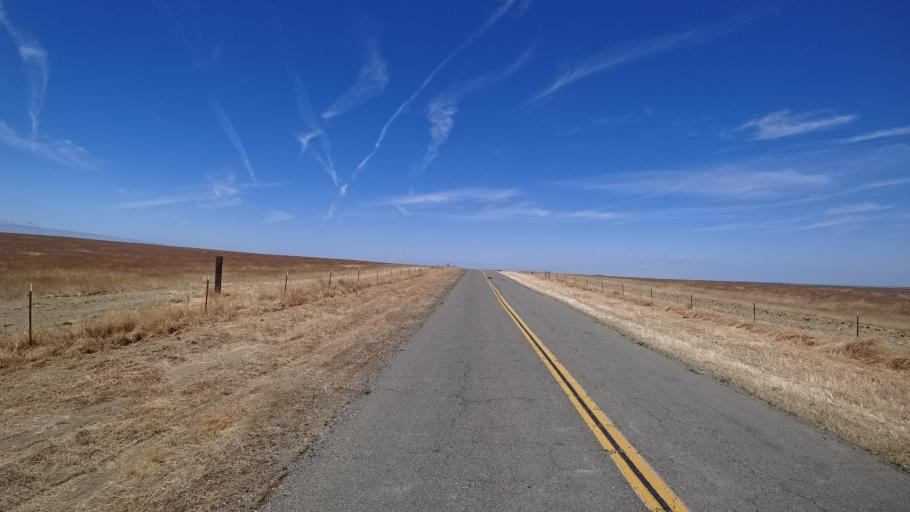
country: US
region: California
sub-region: Kings County
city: Kettleman City
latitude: 35.8013
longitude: -119.8957
